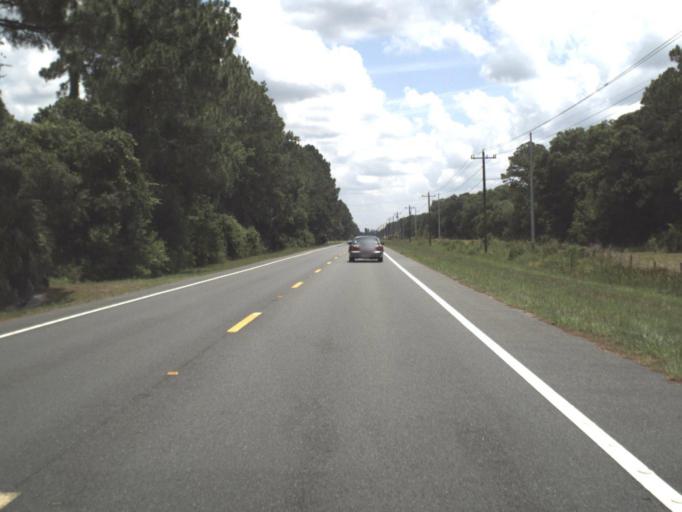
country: US
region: Florida
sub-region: Levy County
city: Chiefland
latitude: 29.2146
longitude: -82.9713
